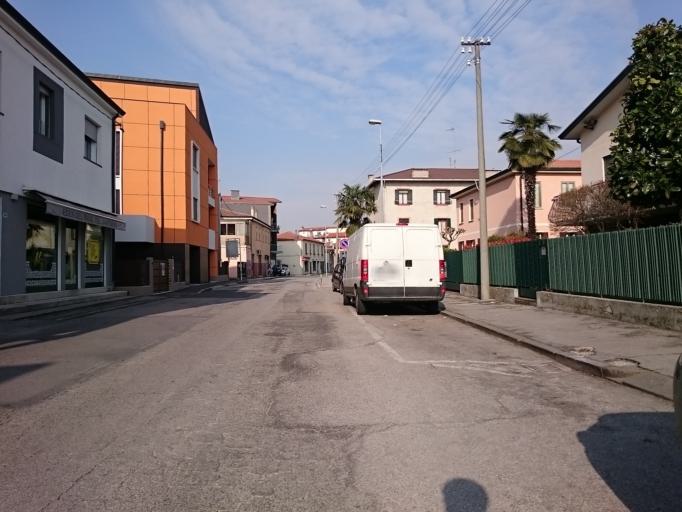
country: IT
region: Veneto
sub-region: Provincia di Padova
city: Padova
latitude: 45.3922
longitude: 11.8842
